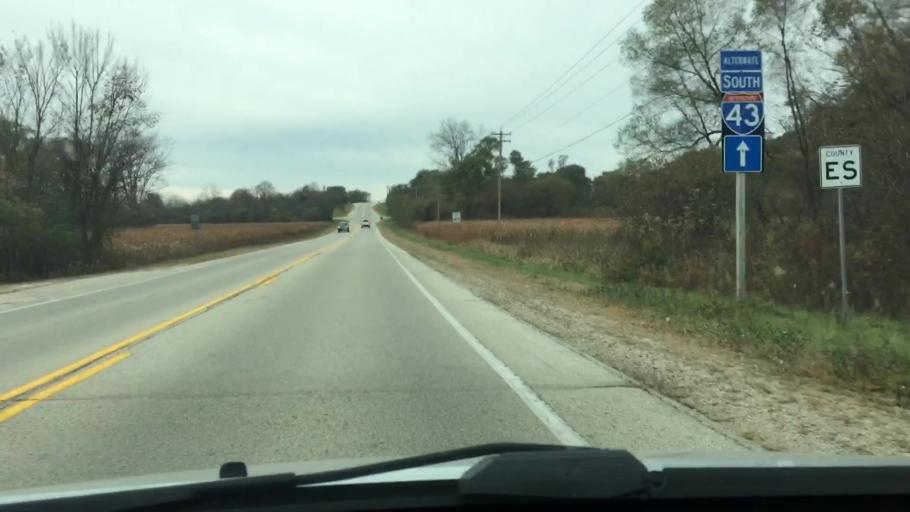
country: US
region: Wisconsin
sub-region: Waukesha County
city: Mukwonago
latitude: 42.8917
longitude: -88.2782
